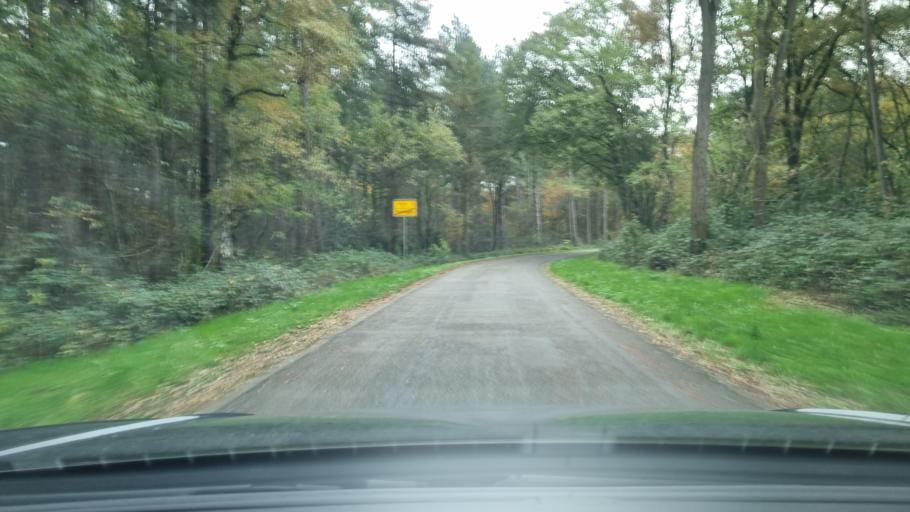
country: DE
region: North Rhine-Westphalia
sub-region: Regierungsbezirk Dusseldorf
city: Kleve
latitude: 51.7955
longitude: 6.0924
